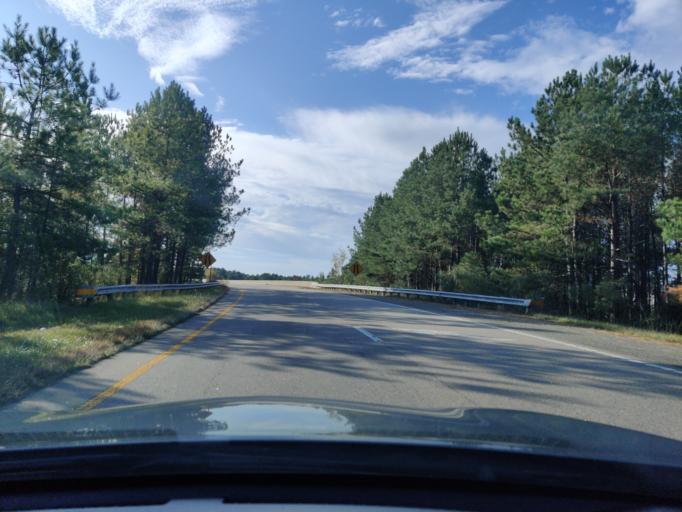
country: US
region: North Carolina
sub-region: Wake County
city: Morrisville
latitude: 35.8916
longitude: -78.8163
